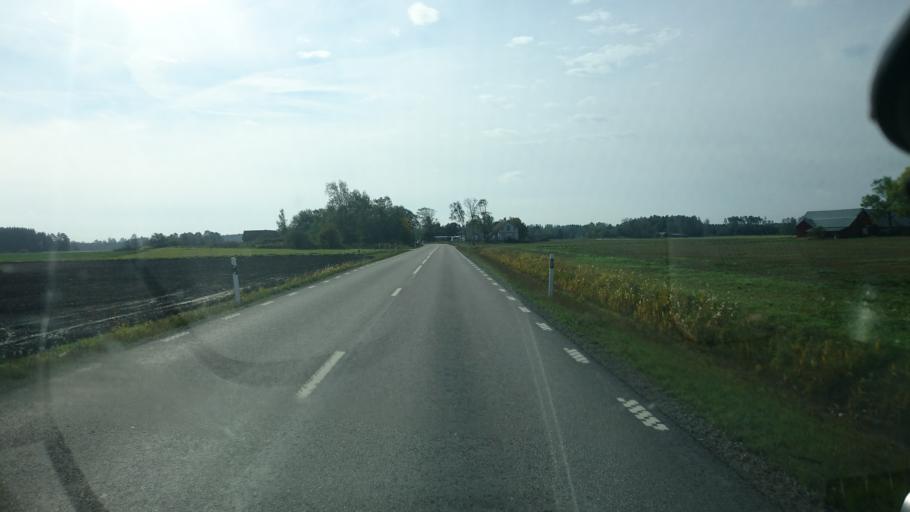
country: SE
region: Vaestra Goetaland
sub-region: Vanersborgs Kommun
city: Vargon
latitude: 58.2705
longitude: 12.3999
